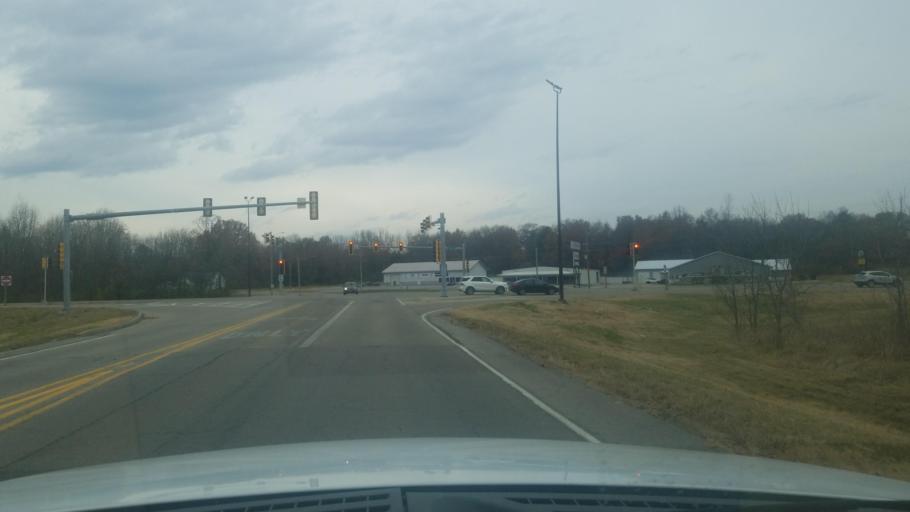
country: US
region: Illinois
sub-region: Saline County
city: Harrisburg
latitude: 37.7375
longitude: -88.5640
